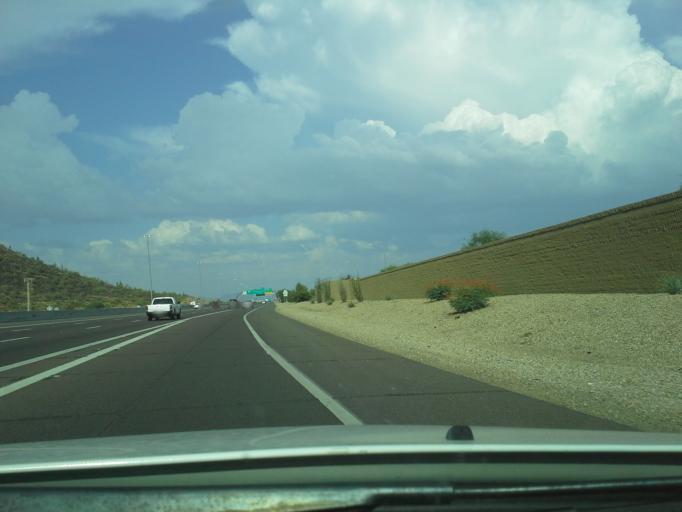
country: US
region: Arizona
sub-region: Maricopa County
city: Peoria
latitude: 33.6692
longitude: -112.1621
